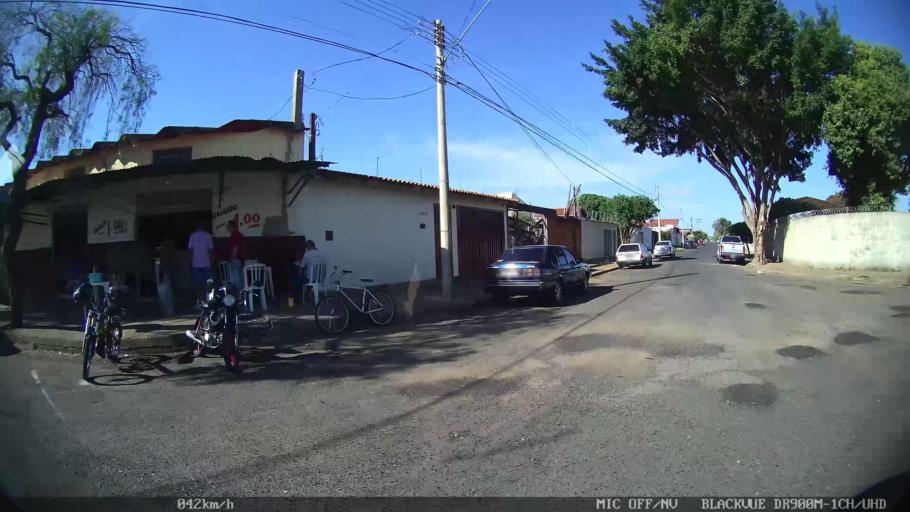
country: BR
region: Sao Paulo
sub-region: Franca
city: Franca
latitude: -20.4894
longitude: -47.4129
